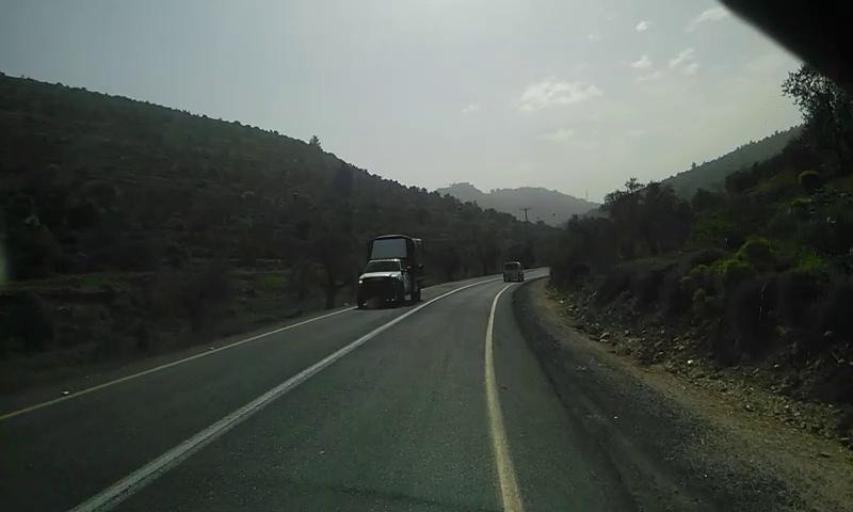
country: PS
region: West Bank
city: Silwad
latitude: 31.9975
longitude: 35.2397
